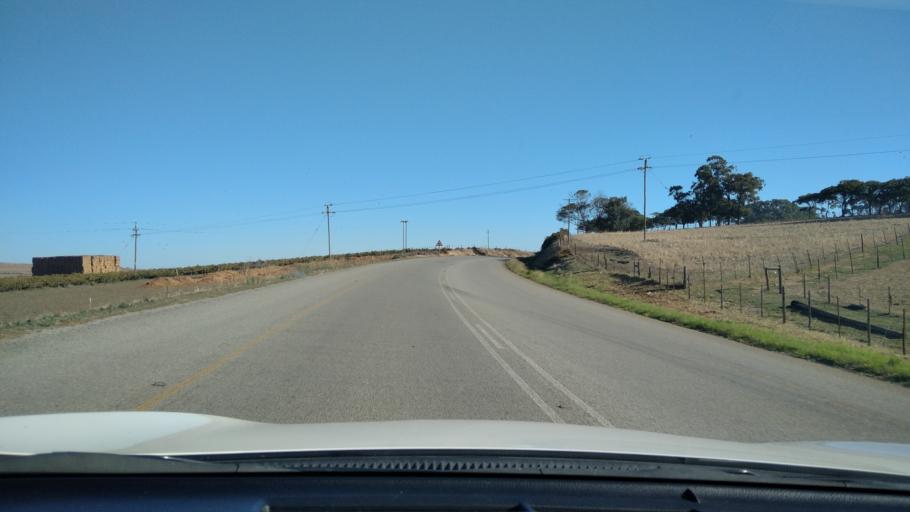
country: ZA
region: Western Cape
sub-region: West Coast District Municipality
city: Malmesbury
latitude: -33.3939
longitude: 18.6737
